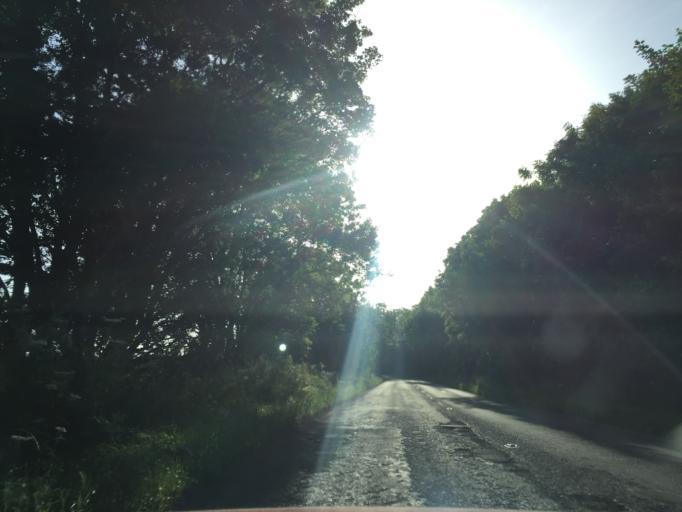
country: GB
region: England
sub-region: Gloucestershire
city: Cirencester
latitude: 51.7187
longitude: -1.9311
